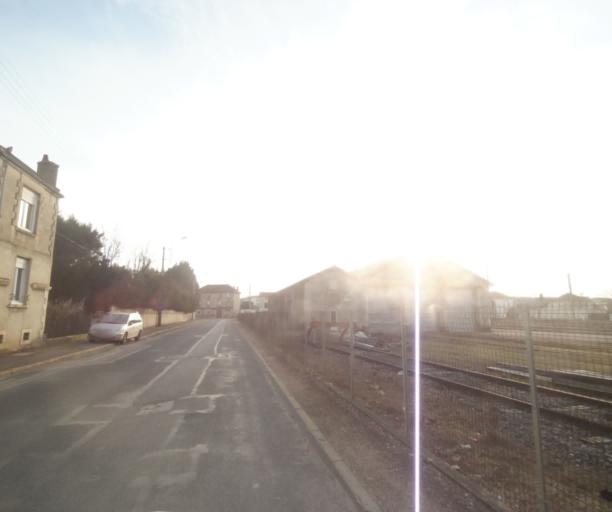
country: FR
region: Champagne-Ardenne
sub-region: Departement de la Haute-Marne
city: Saint-Dizier
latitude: 48.6430
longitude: 4.9490
